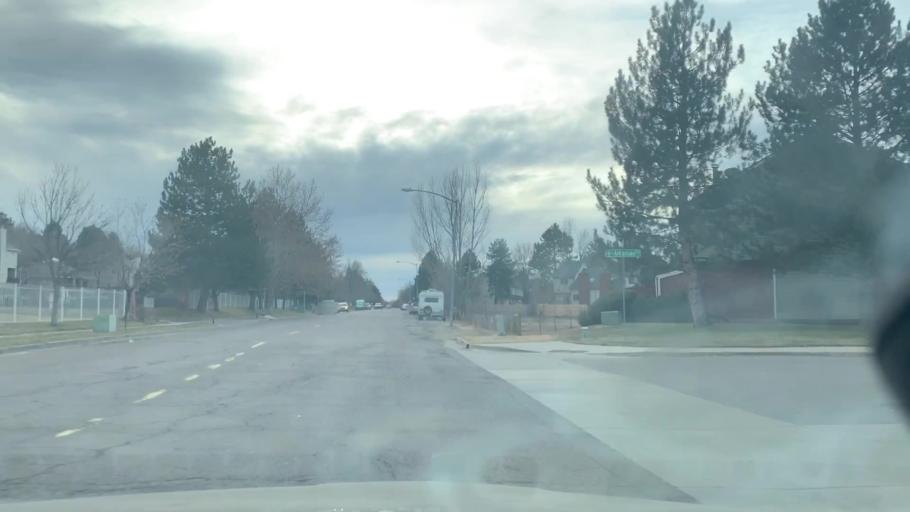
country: US
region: Colorado
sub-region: Arapahoe County
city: Glendale
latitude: 39.6917
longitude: -104.8989
